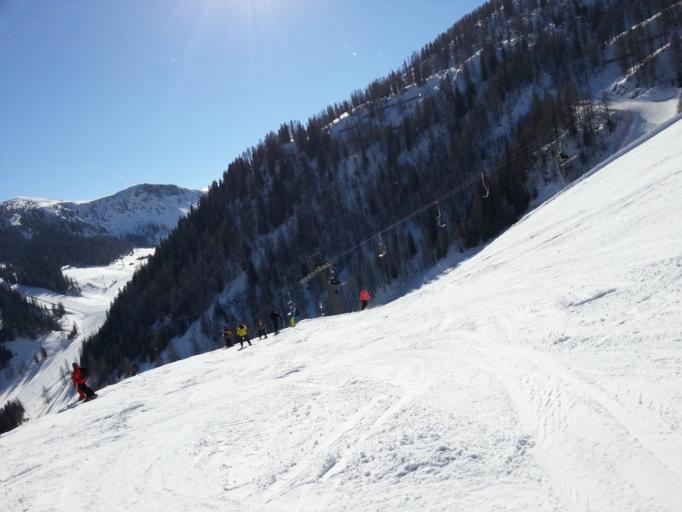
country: AT
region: Salzburg
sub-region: Politischer Bezirk Sankt Johann im Pongau
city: Untertauern
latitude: 47.2918
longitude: 13.4501
